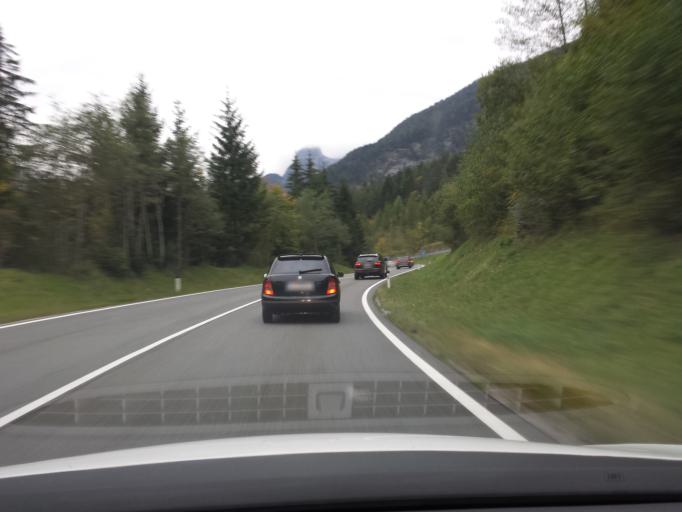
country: AT
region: Salzburg
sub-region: Politischer Bezirk Zell am See
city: Lofer
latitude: 47.5976
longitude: 12.7002
